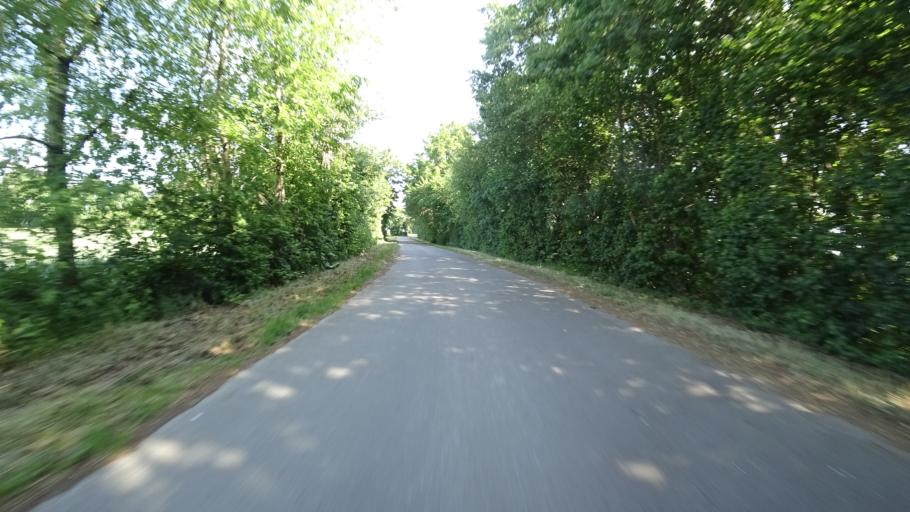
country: DE
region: North Rhine-Westphalia
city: Erwitte
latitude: 51.6176
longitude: 8.3718
